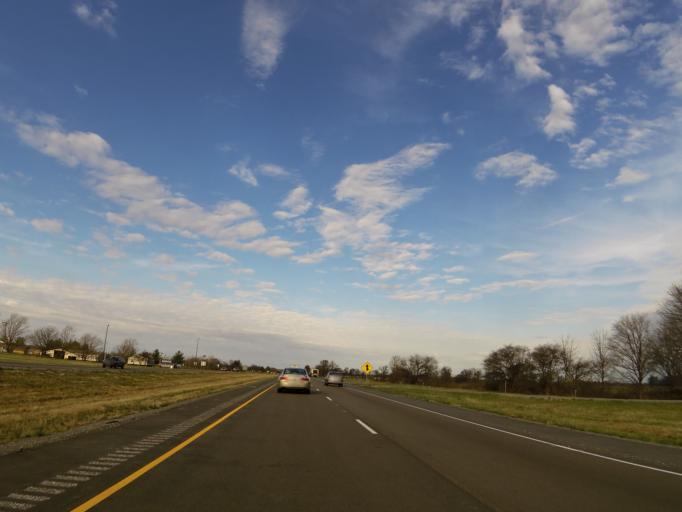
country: US
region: Illinois
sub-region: Washington County
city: Okawville
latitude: 38.4408
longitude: -89.5320
